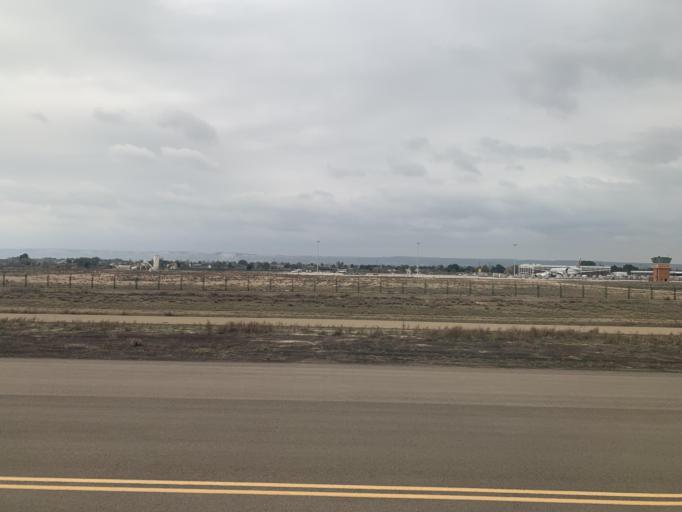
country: ES
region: Aragon
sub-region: Provincia de Zaragoza
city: Utebo
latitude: 41.6625
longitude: -1.0180
